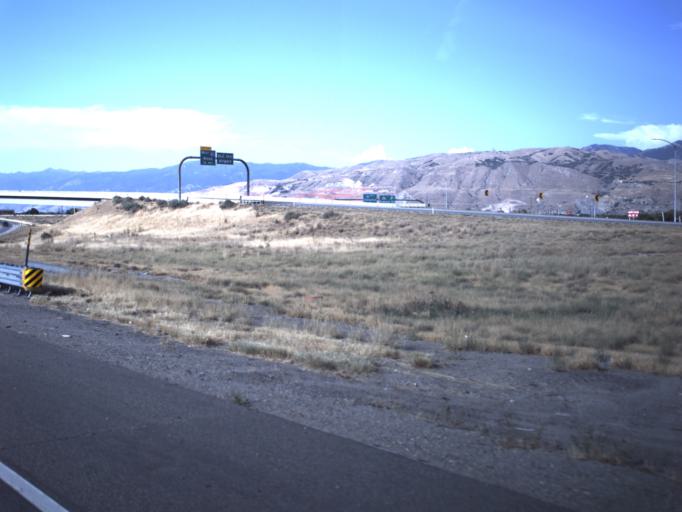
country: US
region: Utah
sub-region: Salt Lake County
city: Salt Lake City
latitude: 40.7614
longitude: -111.9508
